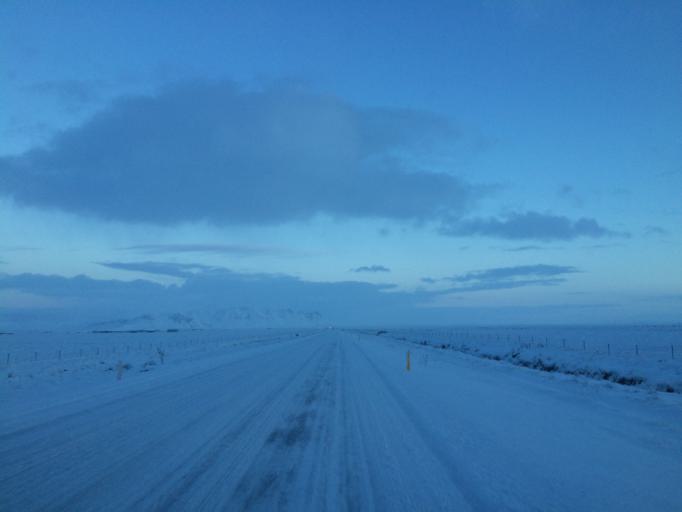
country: IS
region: South
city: Selfoss
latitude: 63.8738
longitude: -21.0951
